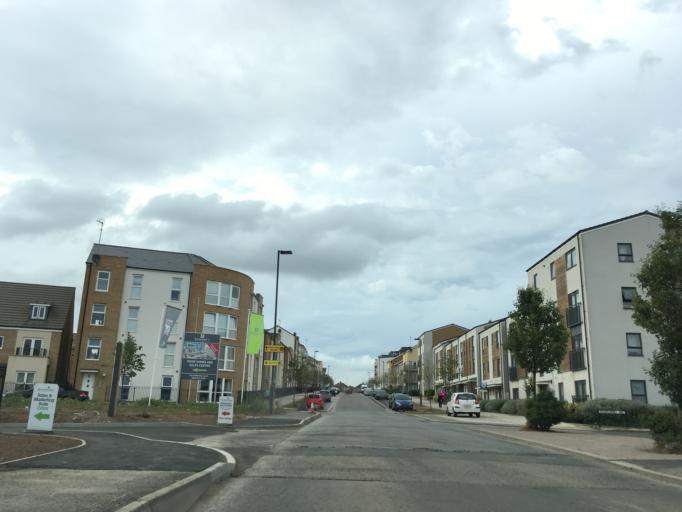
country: GB
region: England
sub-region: South Gloucestershire
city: Almondsbury
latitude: 51.5269
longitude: -2.5755
